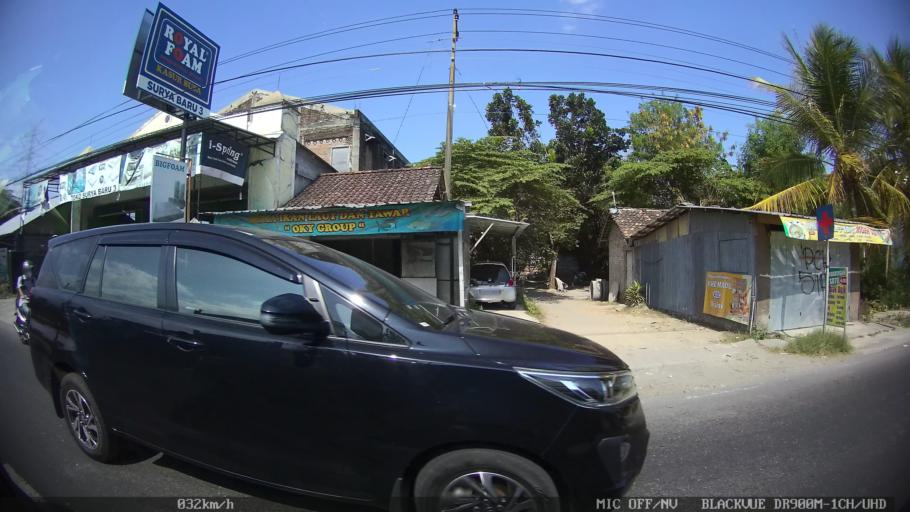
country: ID
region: Daerah Istimewa Yogyakarta
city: Sewon
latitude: -7.8858
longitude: 110.3880
